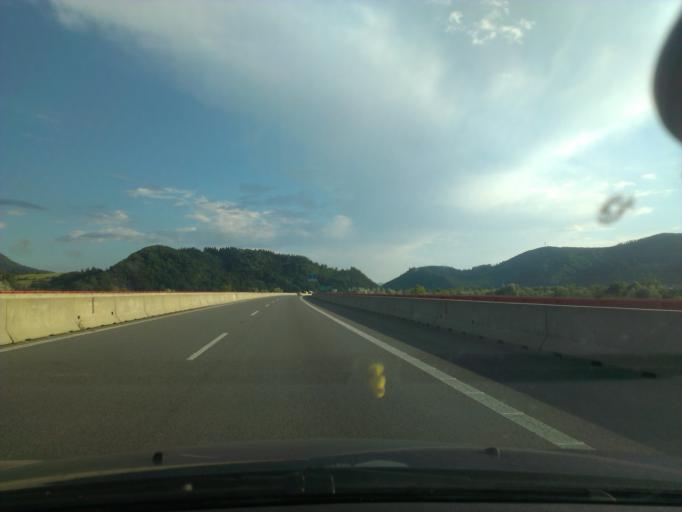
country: SK
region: Trenciansky
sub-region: Okres Povazska Bystrica
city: Povazska Bystrica
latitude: 49.1688
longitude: 18.4796
